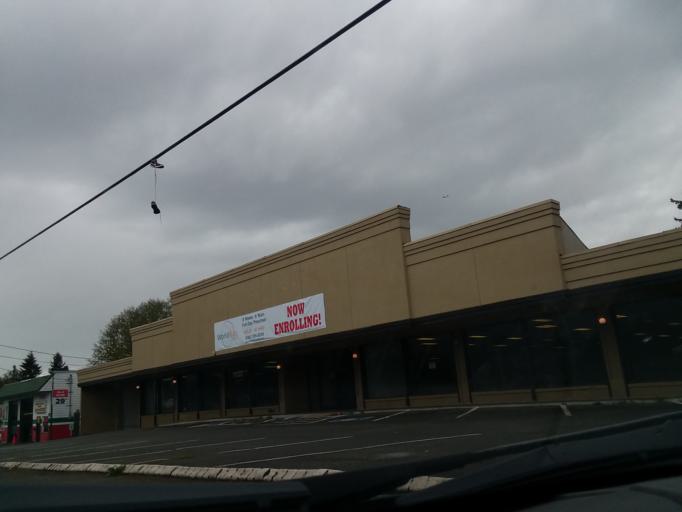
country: US
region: Washington
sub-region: King County
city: Burien
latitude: 47.4823
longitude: -122.3337
